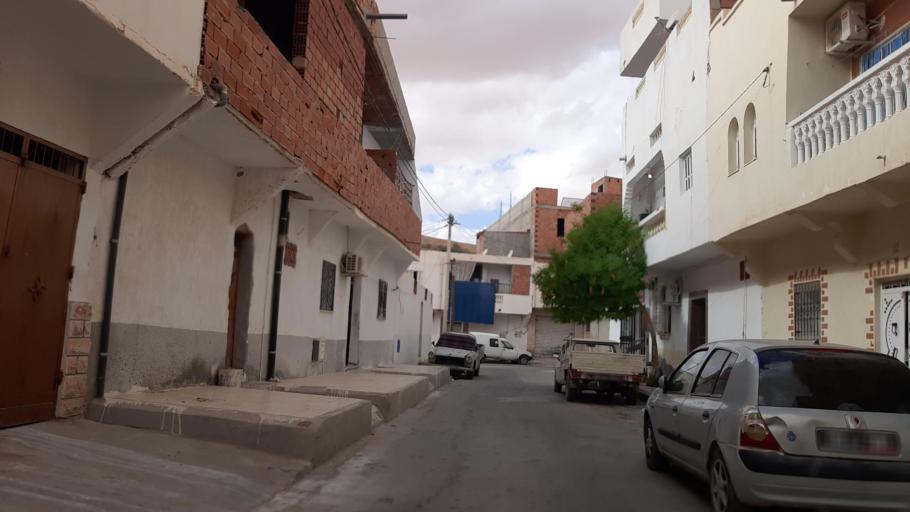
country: TN
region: Tataouine
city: Tataouine
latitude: 32.9315
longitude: 10.4482
